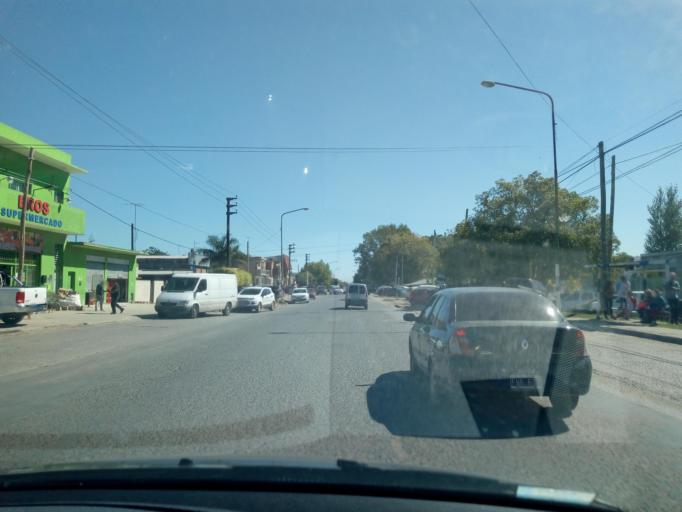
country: AR
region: Buenos Aires
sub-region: Partido de La Plata
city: La Plata
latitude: -35.0001
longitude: -58.0418
